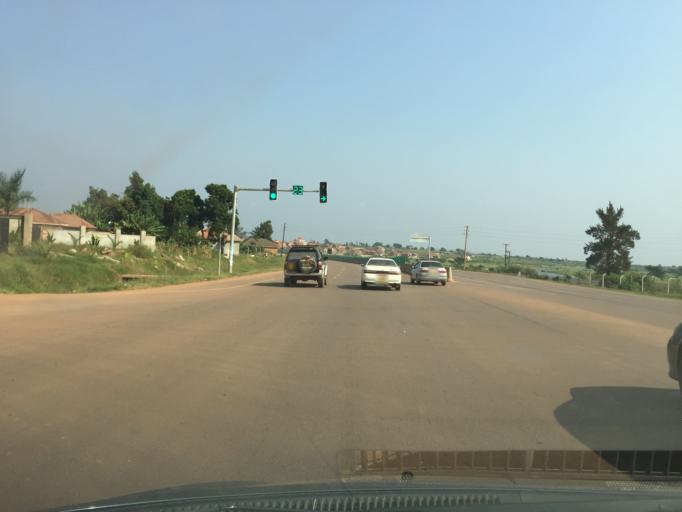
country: UG
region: Central Region
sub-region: Wakiso District
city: Kajansi
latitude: 0.2079
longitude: 32.5886
